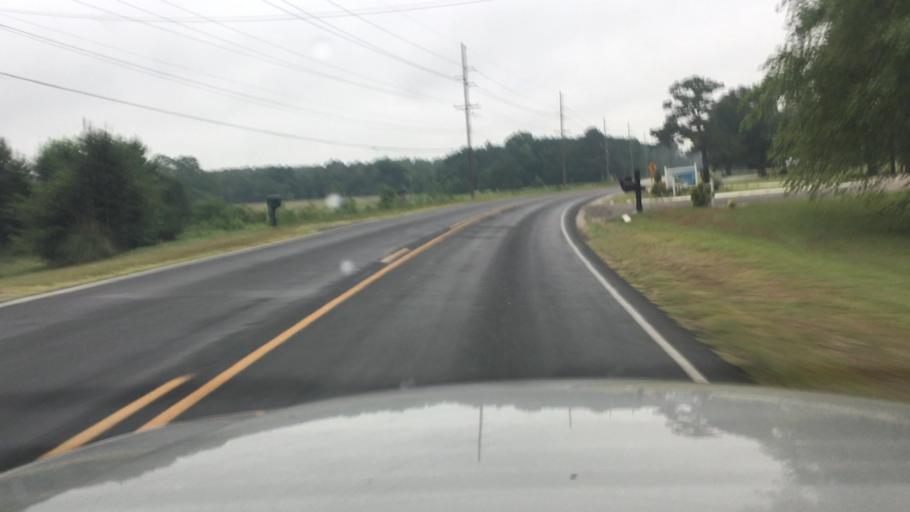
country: US
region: North Carolina
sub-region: Cumberland County
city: Fayetteville
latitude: 35.0073
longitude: -78.8629
